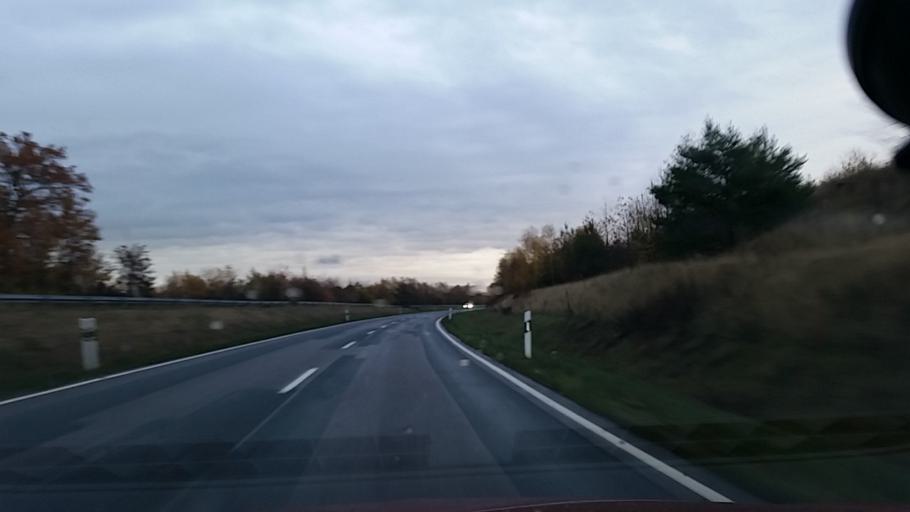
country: DE
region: Lower Saxony
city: Ruhen
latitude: 52.4611
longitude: 10.8378
